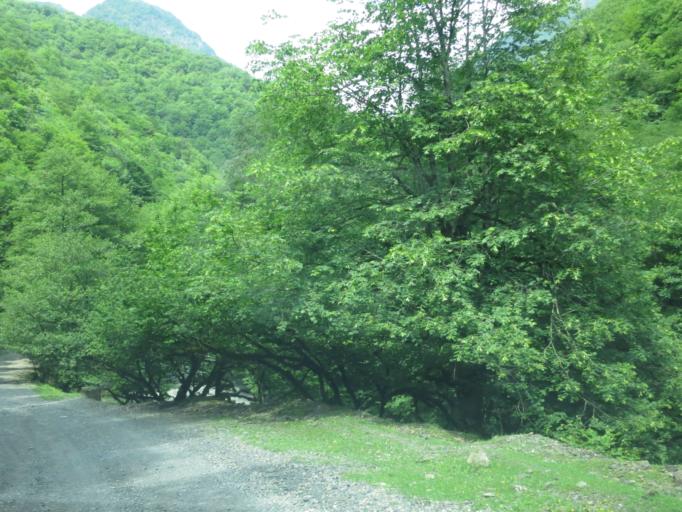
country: GE
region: Kakheti
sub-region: Telavi
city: Telavi
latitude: 42.1916
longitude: 45.4553
